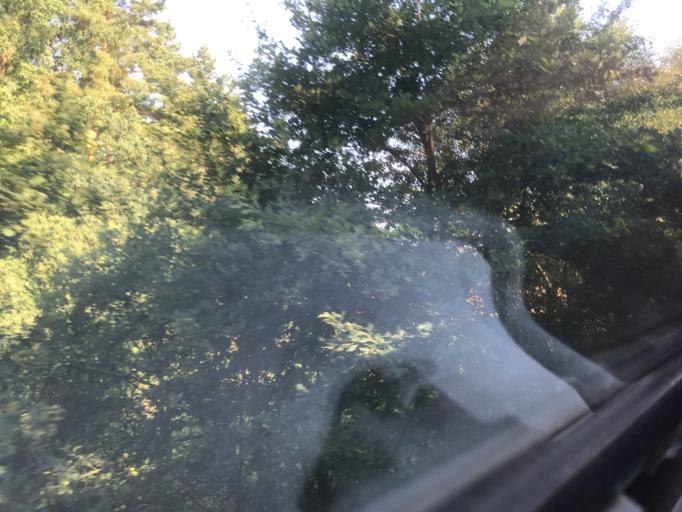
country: CZ
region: Jihocesky
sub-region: Okres Jindrichuv Hradec
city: Lomnice nad Luznici
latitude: 49.1190
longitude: 14.7365
